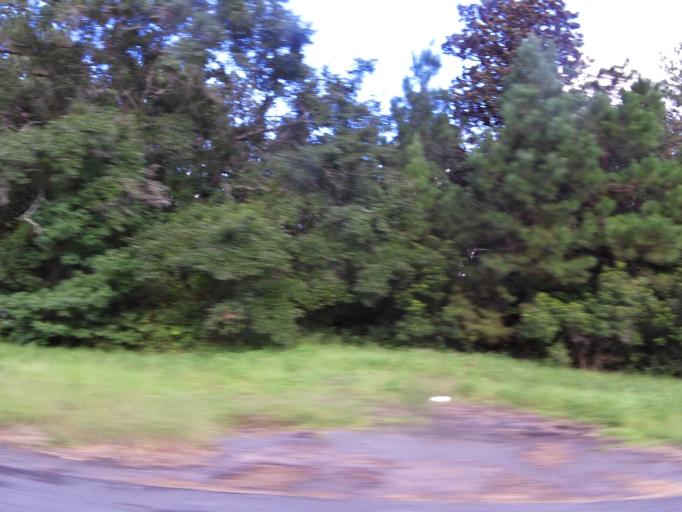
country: US
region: Georgia
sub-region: Camden County
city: Woodbine
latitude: 30.9350
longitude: -81.7169
